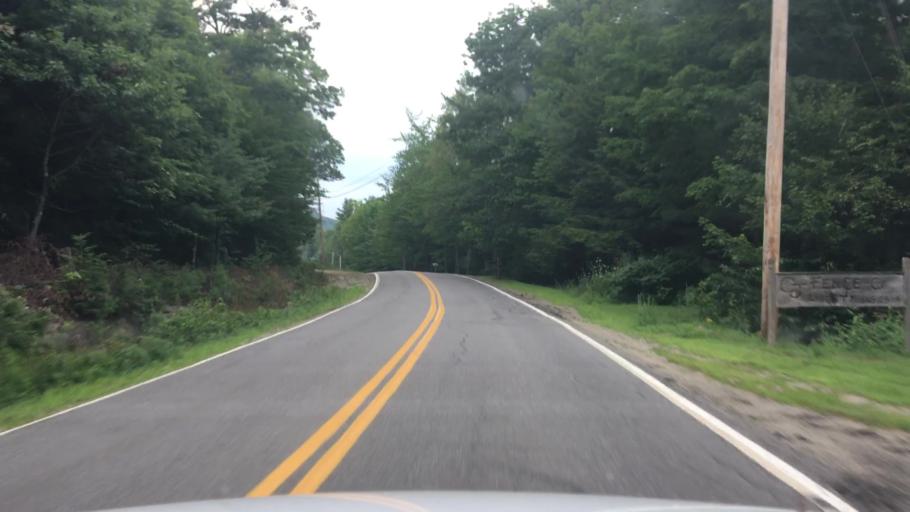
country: US
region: Maine
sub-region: Knox County
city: Washington
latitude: 44.3376
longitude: -69.3442
